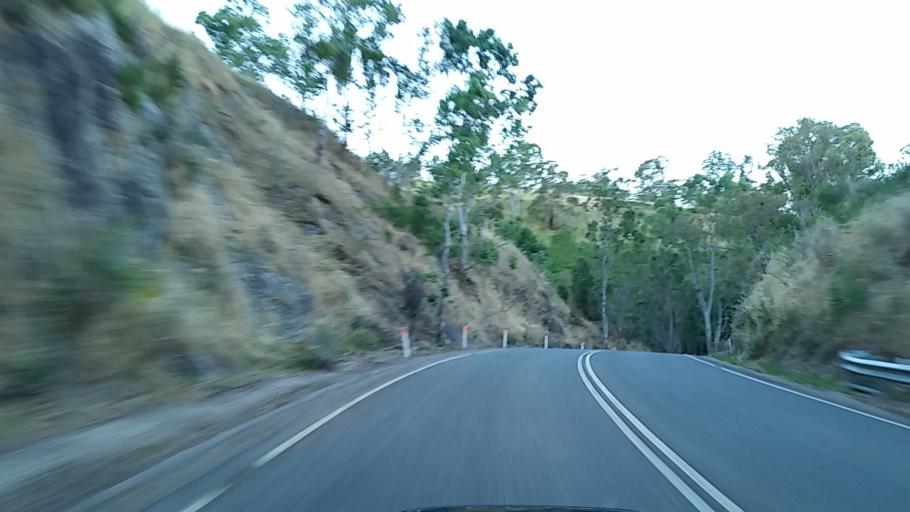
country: AU
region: South Australia
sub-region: Tea Tree Gully
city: Golden Grove
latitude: -34.8513
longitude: 138.7910
